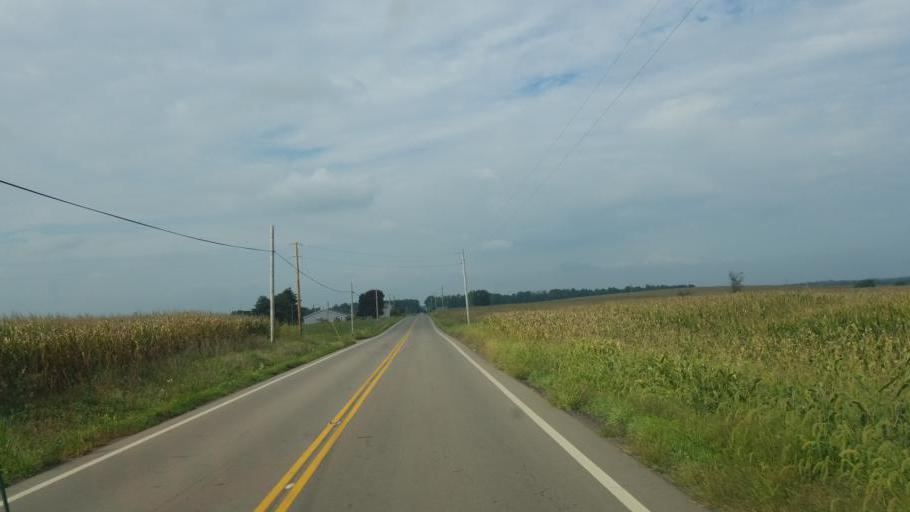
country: US
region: Ohio
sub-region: Wayne County
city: West Salem
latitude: 40.8773
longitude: -82.0535
